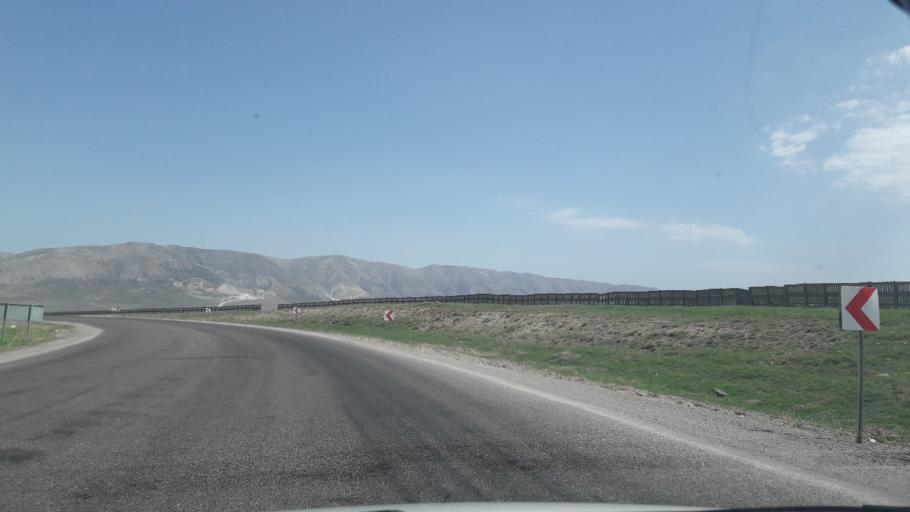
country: TR
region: Sivas
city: Deliktas
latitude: 39.3423
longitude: 37.1479
